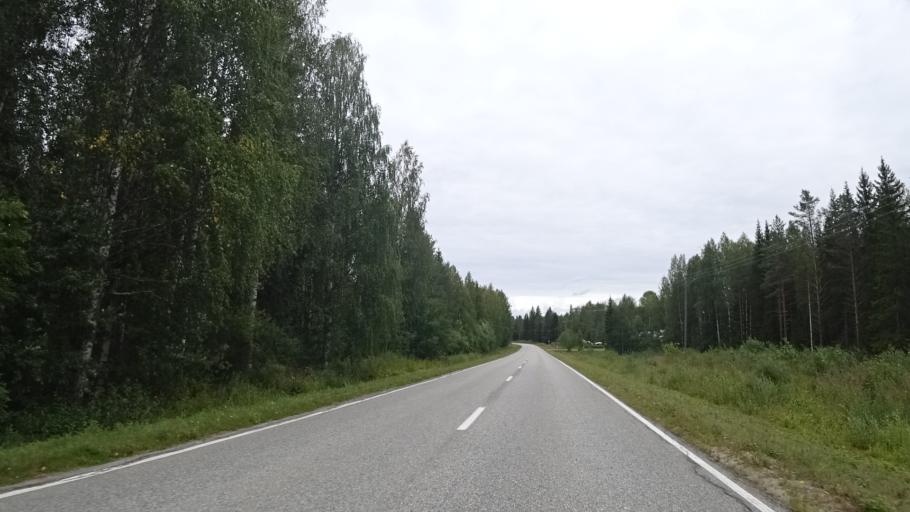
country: FI
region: North Karelia
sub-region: Joensuu
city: Ilomantsi
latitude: 62.6355
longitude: 31.2819
